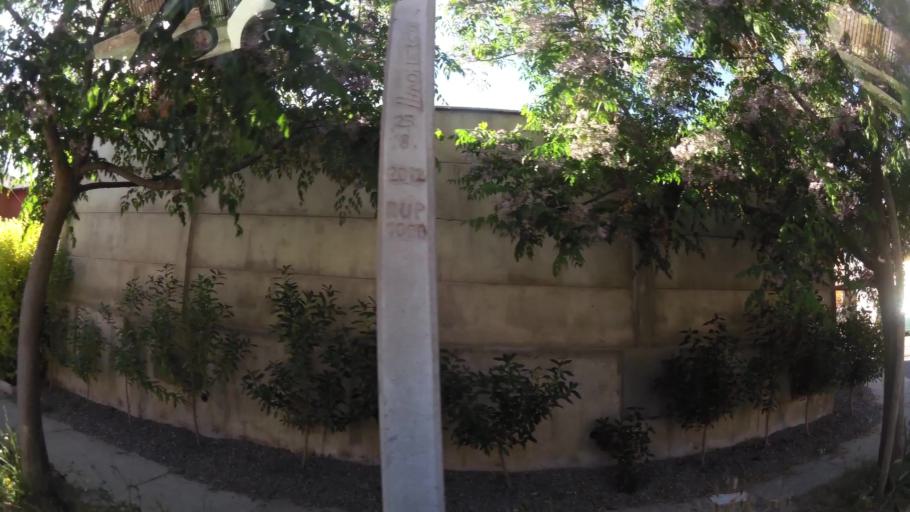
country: CL
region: Valparaiso
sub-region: Provincia de Valparaiso
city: Valparaiso
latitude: -33.1229
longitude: -71.5827
